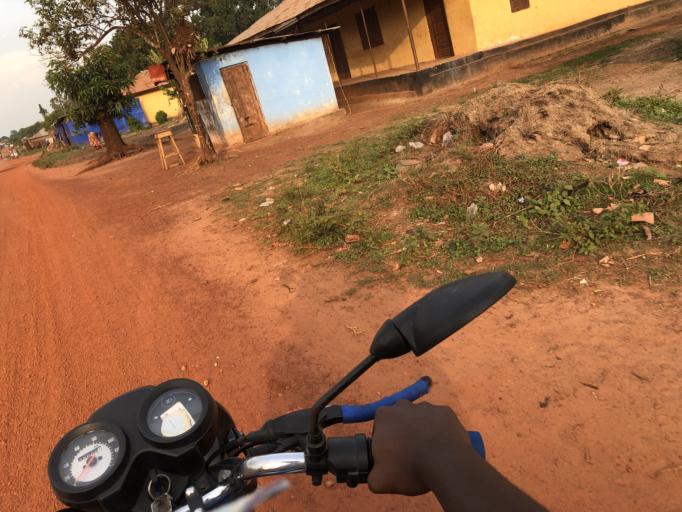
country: SL
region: Northern Province
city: Yonibana
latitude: 8.4676
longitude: -12.2072
